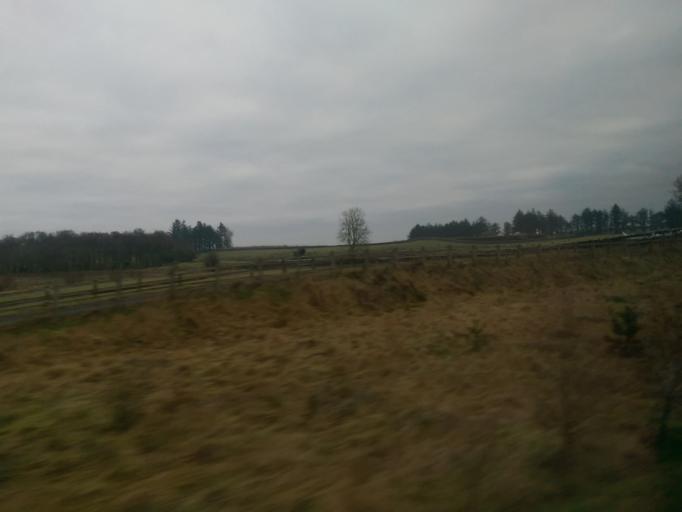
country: IE
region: Connaught
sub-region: County Galway
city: Loughrea
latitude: 53.2825
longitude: -8.4453
